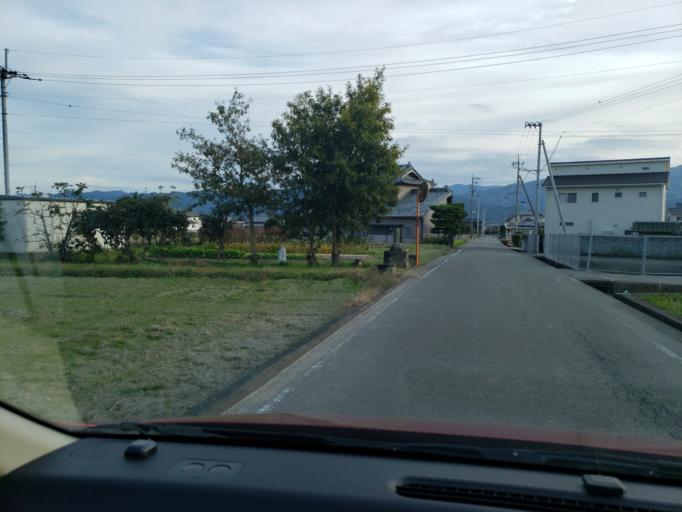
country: JP
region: Tokushima
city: Wakimachi
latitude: 34.0907
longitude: 134.2260
